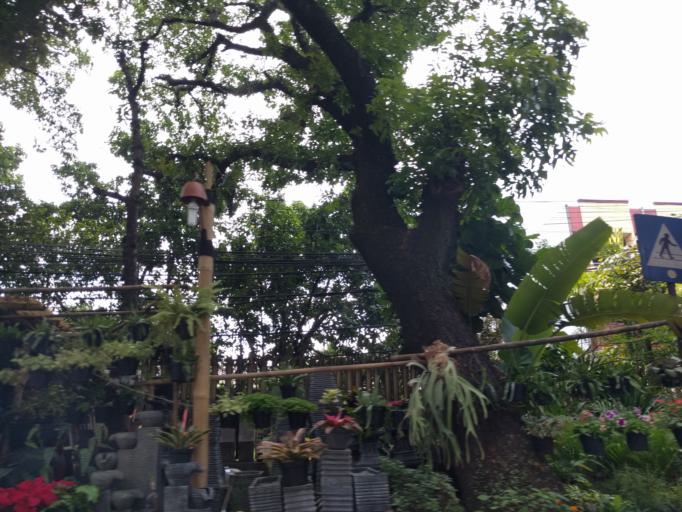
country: ID
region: West Java
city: Bogor
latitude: -6.6188
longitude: 106.8157
